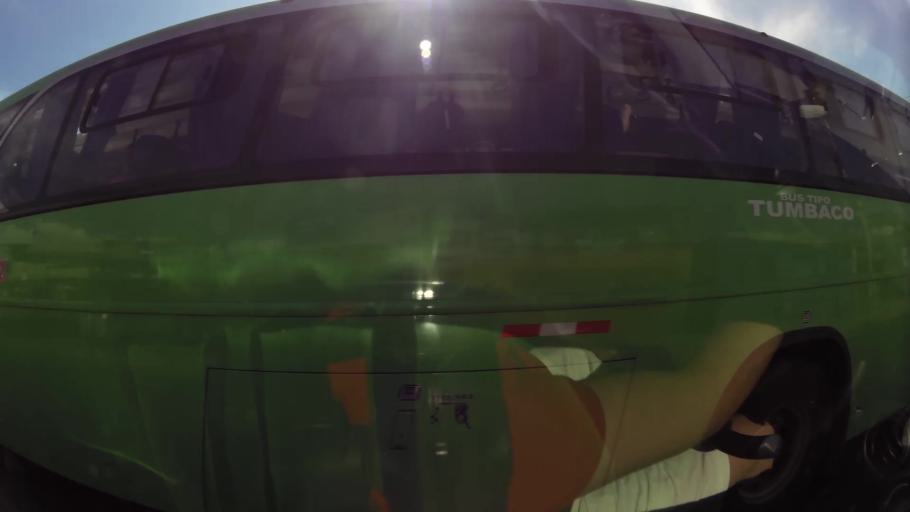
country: EC
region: Pichincha
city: Quito
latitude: -0.2001
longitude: -78.4337
